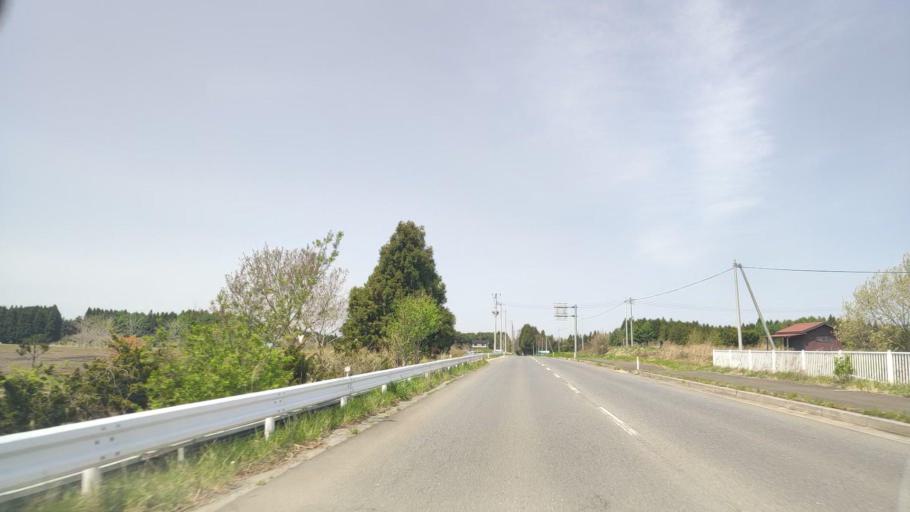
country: JP
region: Aomori
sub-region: Hachinohe Shi
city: Uchimaru
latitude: 40.5290
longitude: 141.4074
